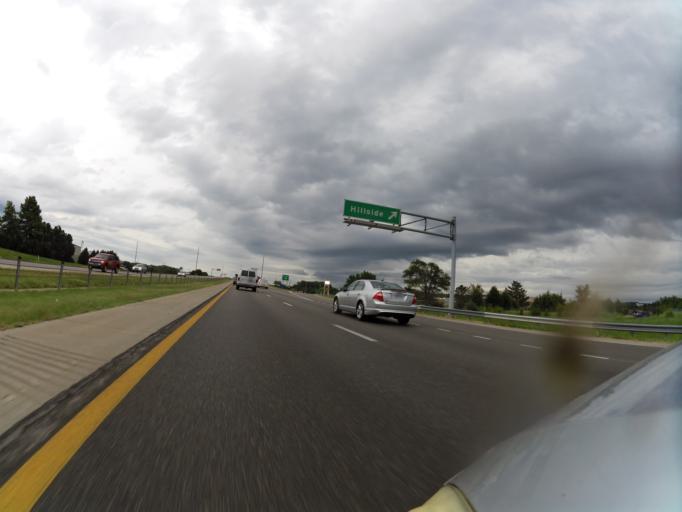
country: US
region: Kansas
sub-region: Sedgwick County
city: Bellaire
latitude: 37.7435
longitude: -97.3027
